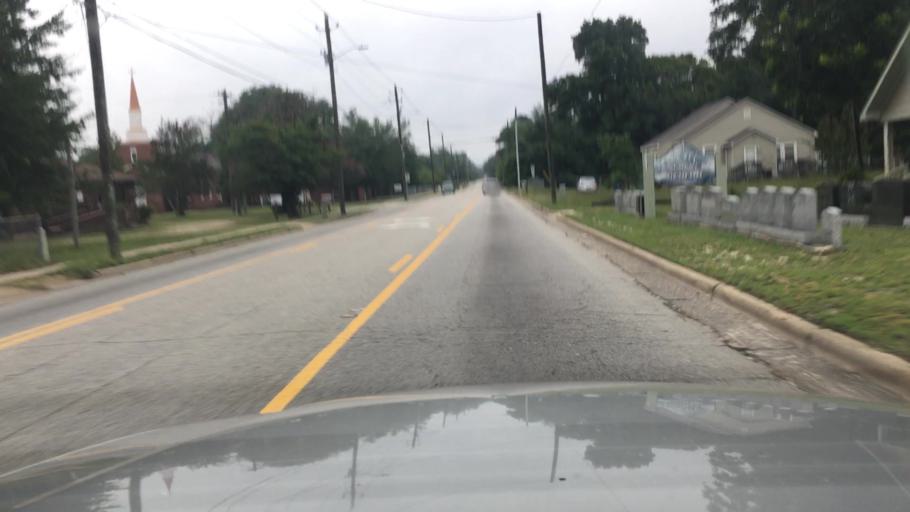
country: US
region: North Carolina
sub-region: Cumberland County
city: Fayetteville
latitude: 35.0232
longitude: -78.9002
